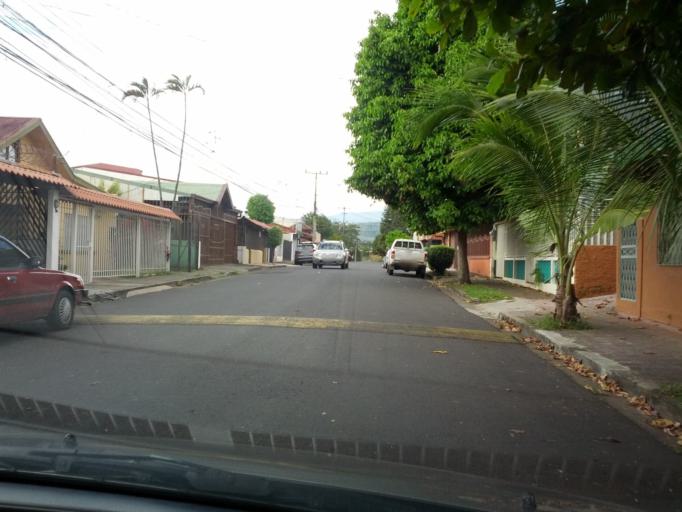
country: CR
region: Alajuela
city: Alajuela
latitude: 10.0219
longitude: -84.2131
